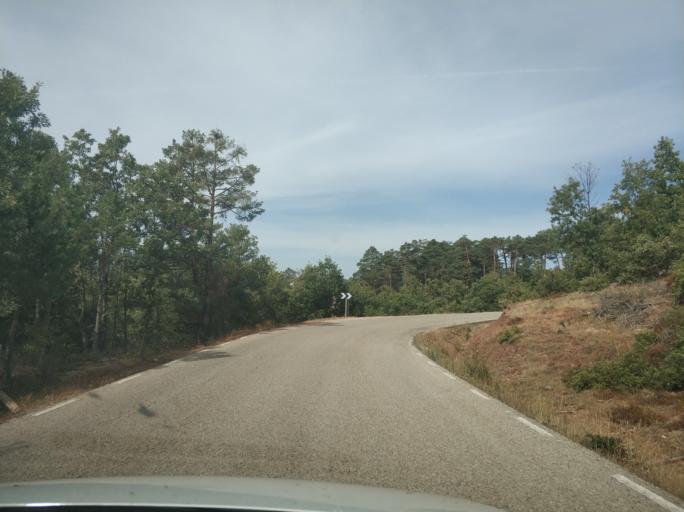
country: ES
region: Castille and Leon
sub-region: Provincia de Soria
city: Duruelo de la Sierra
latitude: 41.9071
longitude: -2.9436
